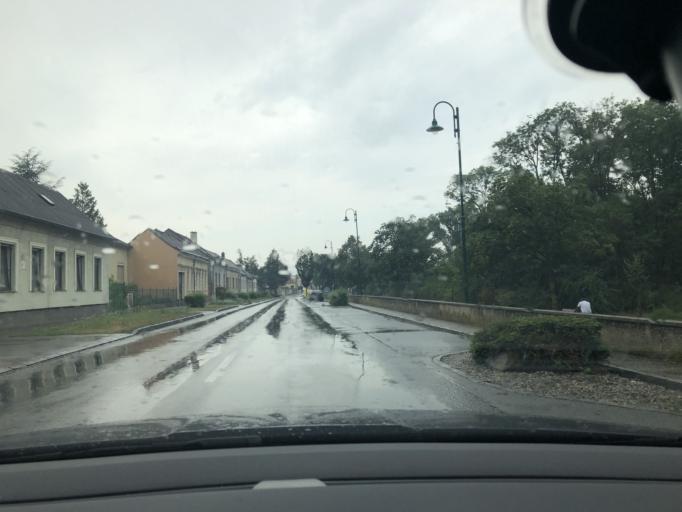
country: AT
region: Lower Austria
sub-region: Politischer Bezirk Ganserndorf
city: Ganserndorf
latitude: 48.3681
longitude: 16.6921
